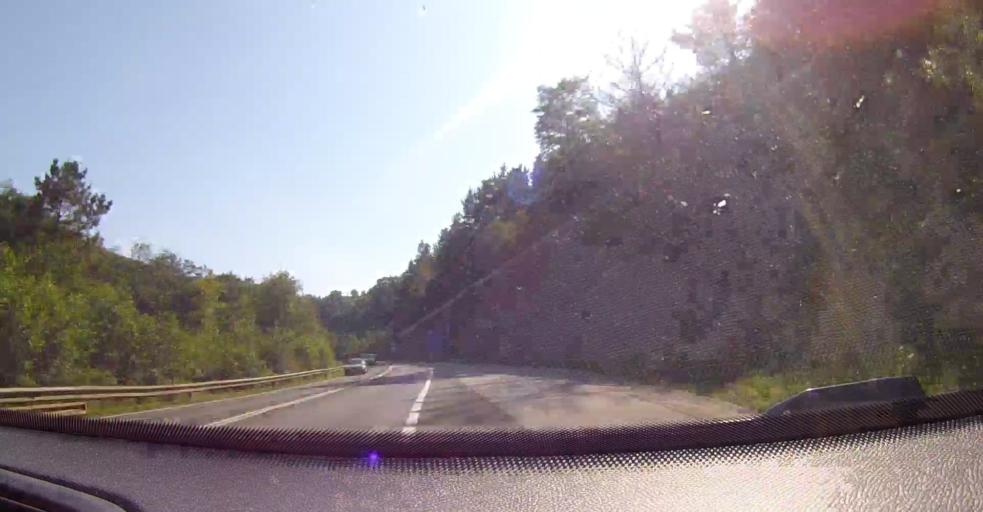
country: ES
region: Basque Country
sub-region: Bizkaia
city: Muxika
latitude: 43.2595
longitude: -2.6896
